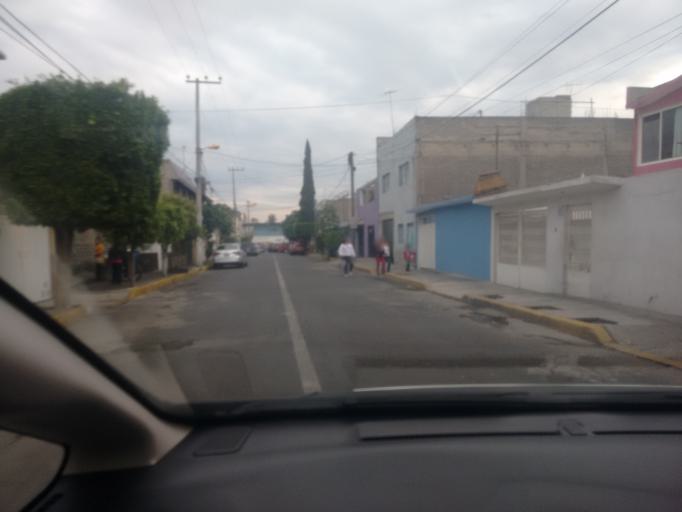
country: MX
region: Mexico City
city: Gustavo A. Madero
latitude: 19.4840
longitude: -99.0450
